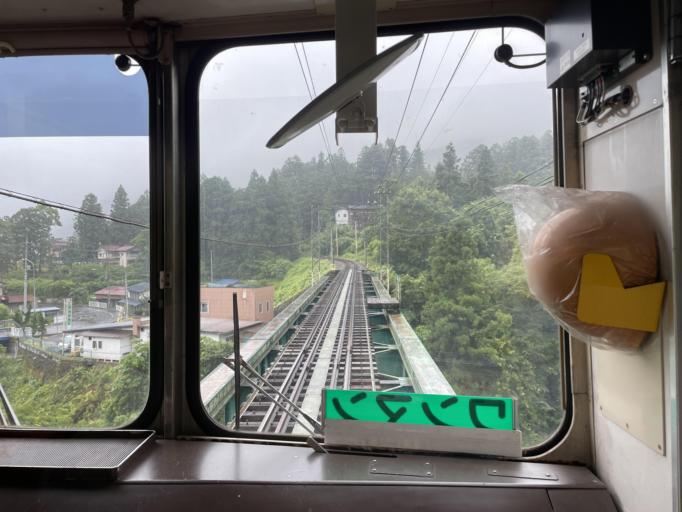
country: JP
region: Saitama
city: Chichibu
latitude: 35.9532
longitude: 139.0257
